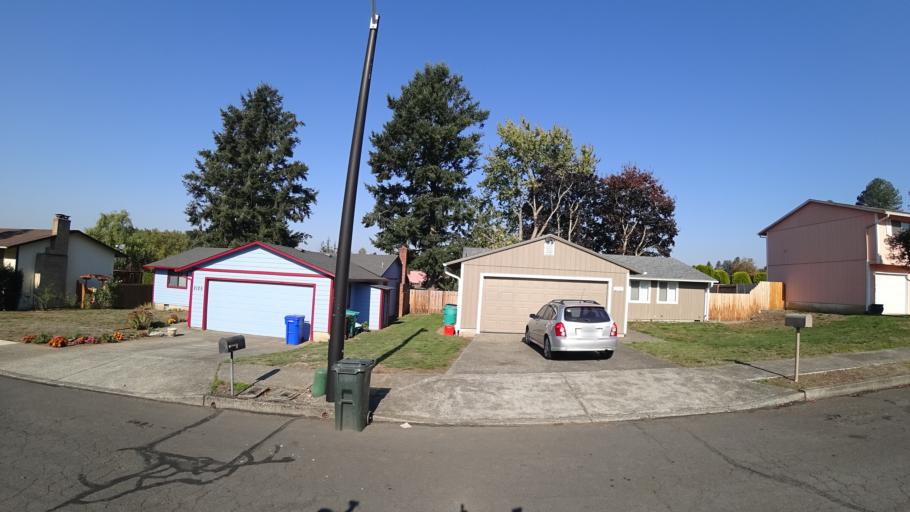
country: US
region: Oregon
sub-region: Multnomah County
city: Gresham
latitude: 45.4910
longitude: -122.4536
